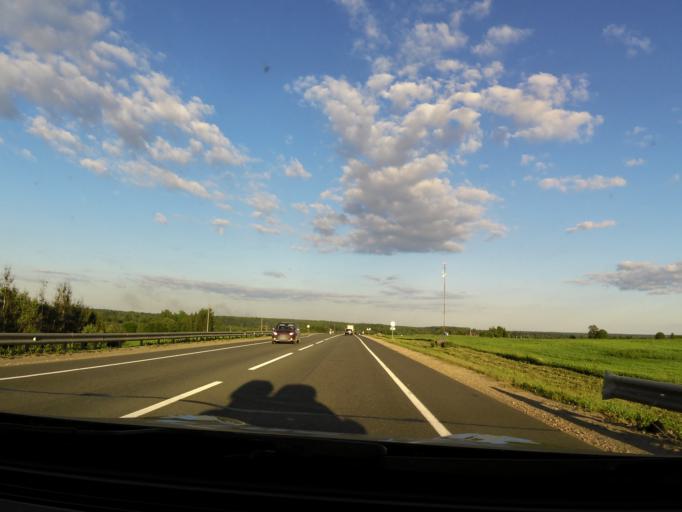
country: RU
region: Vologda
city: Vologda
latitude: 59.0609
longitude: 40.0568
